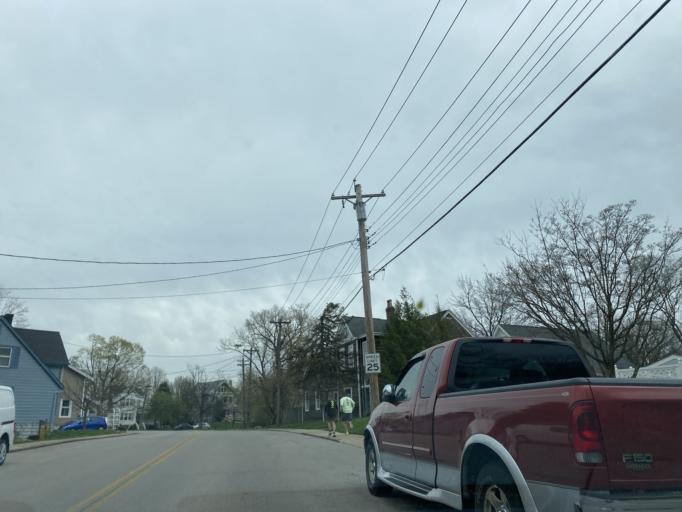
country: US
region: Kentucky
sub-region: Campbell County
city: Fort Thomas
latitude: 39.0940
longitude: -84.4494
